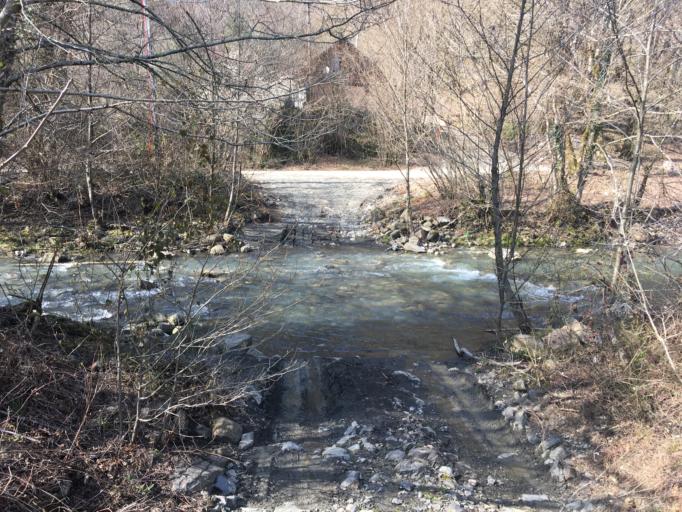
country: RU
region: Krasnodarskiy
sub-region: Sochi City
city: Sochi
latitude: 43.6335
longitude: 39.8209
